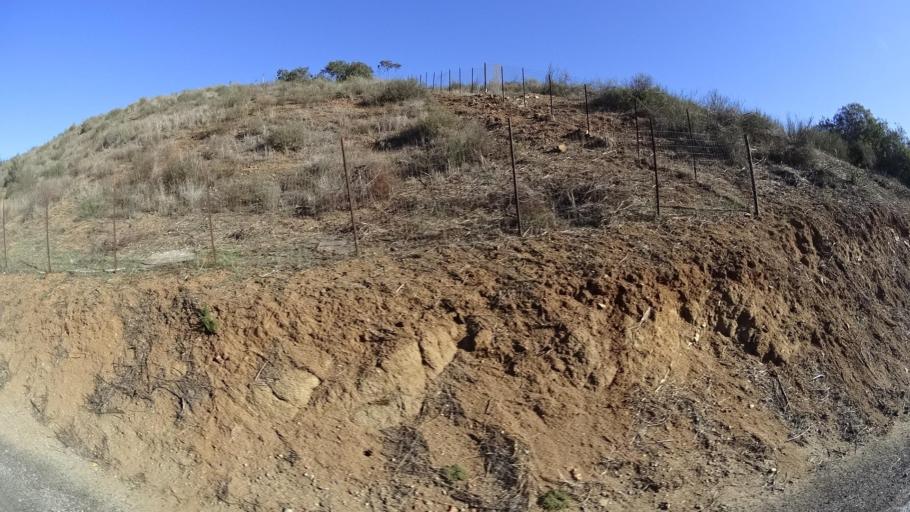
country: MX
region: Baja California
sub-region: Tijuana
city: Villa del Campo
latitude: 32.6236
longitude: -116.7499
